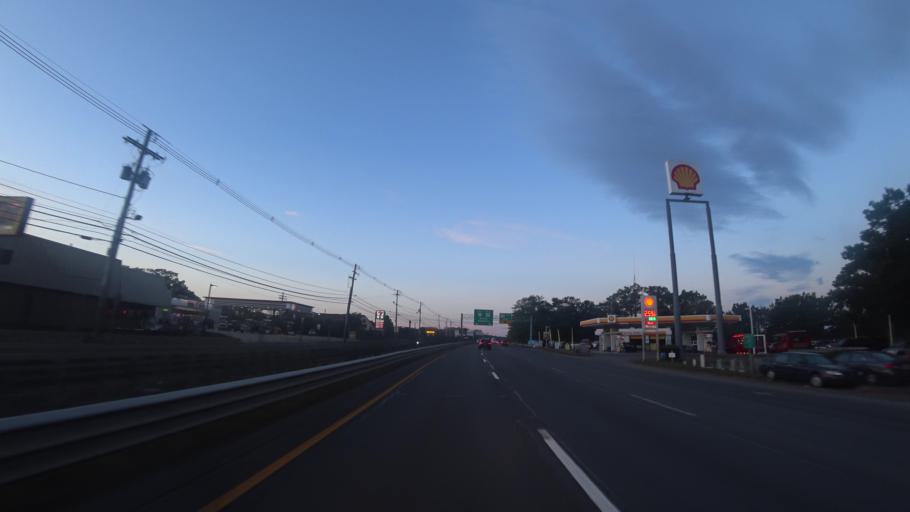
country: US
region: Massachusetts
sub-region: Essex County
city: South Peabody
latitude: 42.5233
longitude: -70.9965
